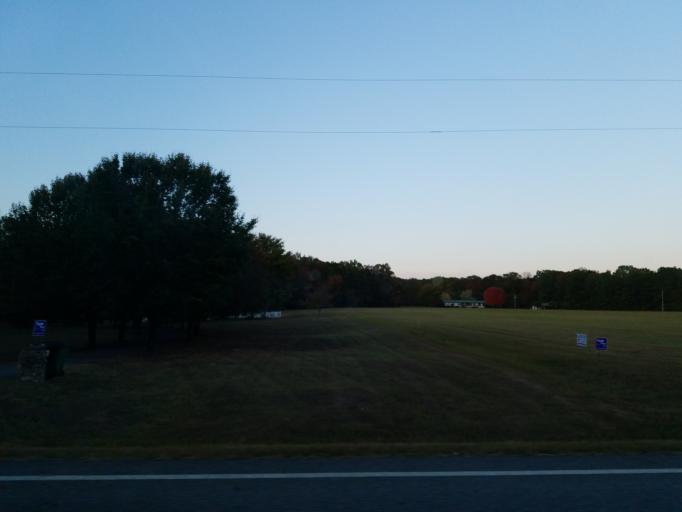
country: US
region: Georgia
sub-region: Gordon County
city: Calhoun
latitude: 34.5961
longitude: -85.0304
